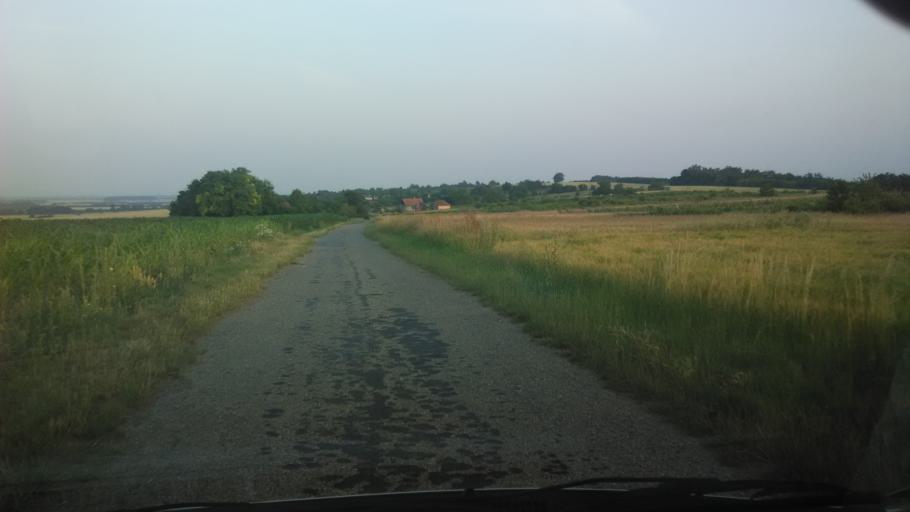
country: SK
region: Nitriansky
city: Levice
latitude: 48.1237
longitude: 18.4519
